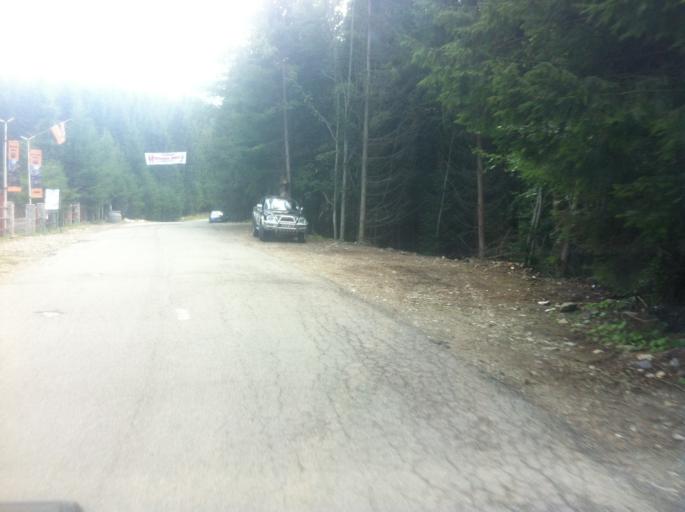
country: RO
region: Hunedoara
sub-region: Oras Petrila
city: Petrila
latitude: 45.4067
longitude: 23.5601
